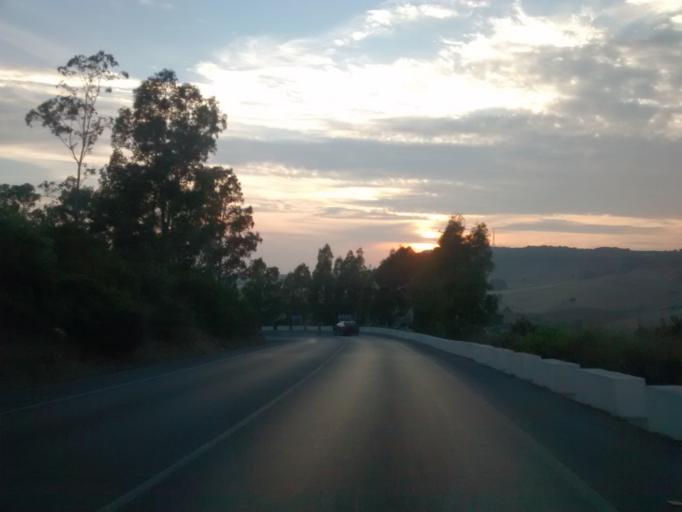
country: ES
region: Andalusia
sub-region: Provincia de Cadiz
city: Vejer de la Frontera
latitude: 36.2565
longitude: -5.9740
